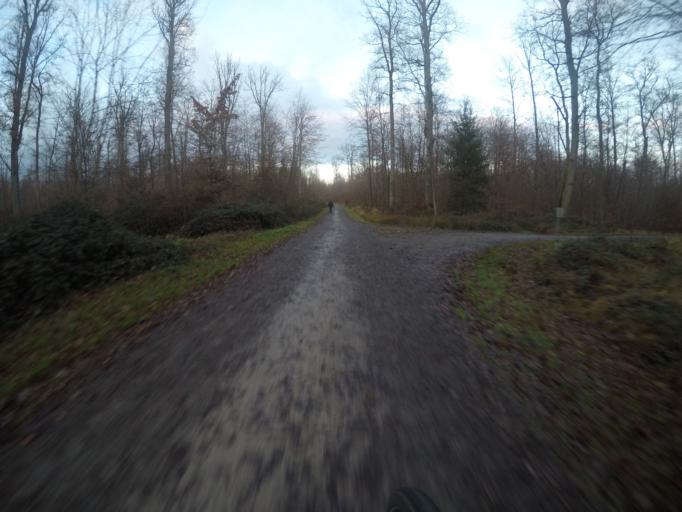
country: DE
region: Baden-Wuerttemberg
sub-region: Tuebingen Region
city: Dettenhausen
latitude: 48.5677
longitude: 9.1072
